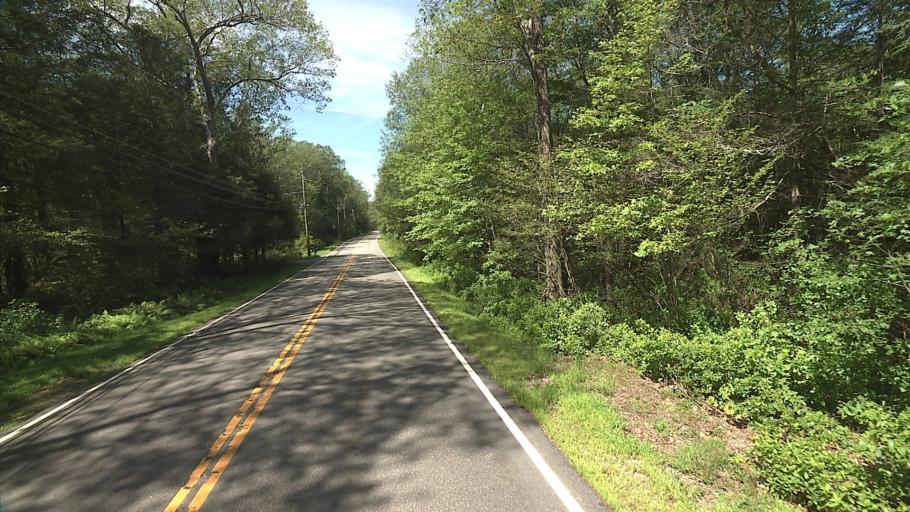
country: US
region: Connecticut
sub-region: Windham County
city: South Woodstock
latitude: 41.8959
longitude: -72.0423
